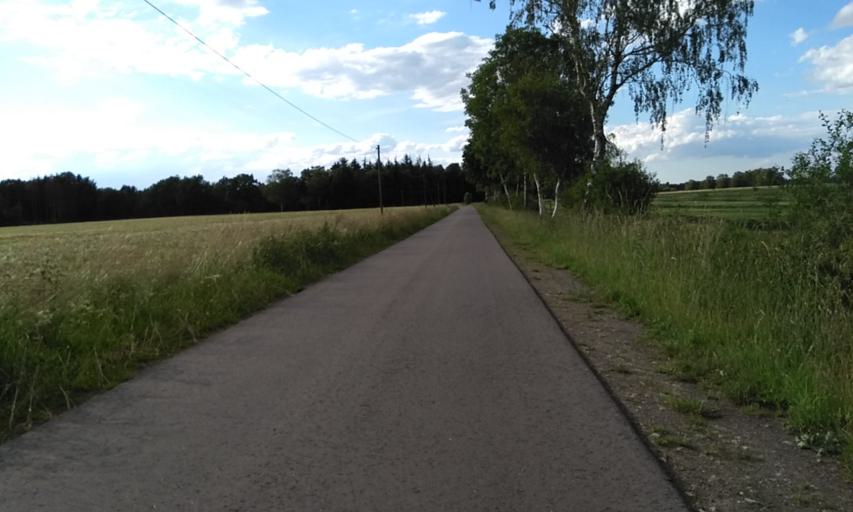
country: DE
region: Lower Saxony
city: Vierden
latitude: 53.3590
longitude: 9.4649
